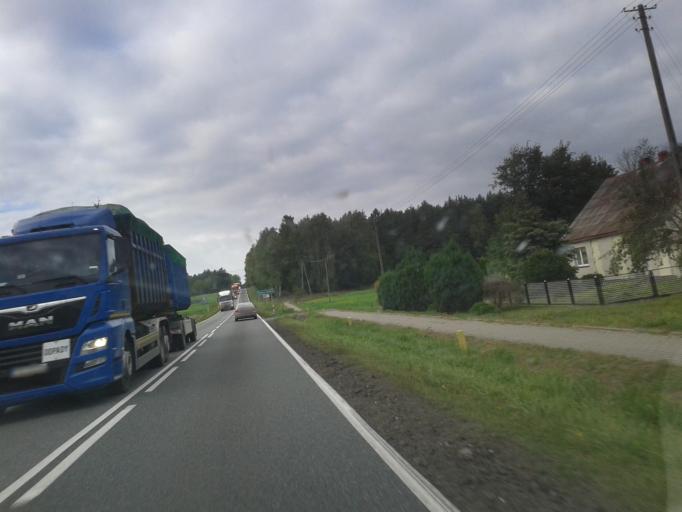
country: PL
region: Kujawsko-Pomorskie
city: Kamien Krajenski
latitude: 53.5426
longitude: 17.5156
